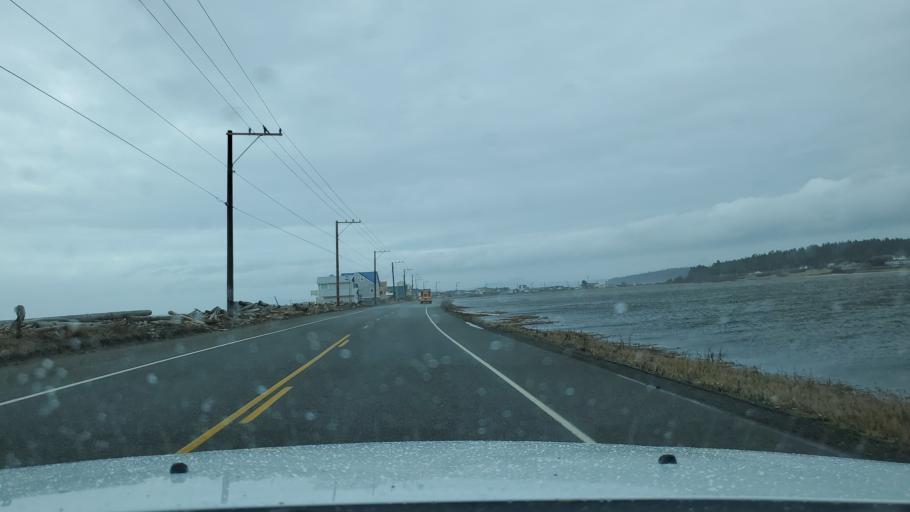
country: US
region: Washington
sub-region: Island County
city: Ault Field
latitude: 48.2992
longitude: -122.7244
